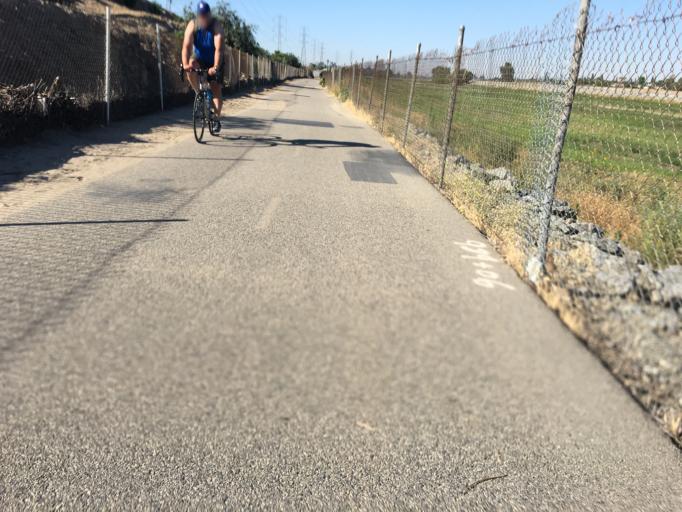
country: US
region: California
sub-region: Los Angeles County
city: West Whittier-Los Nietos
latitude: 33.9925
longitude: -118.0731
